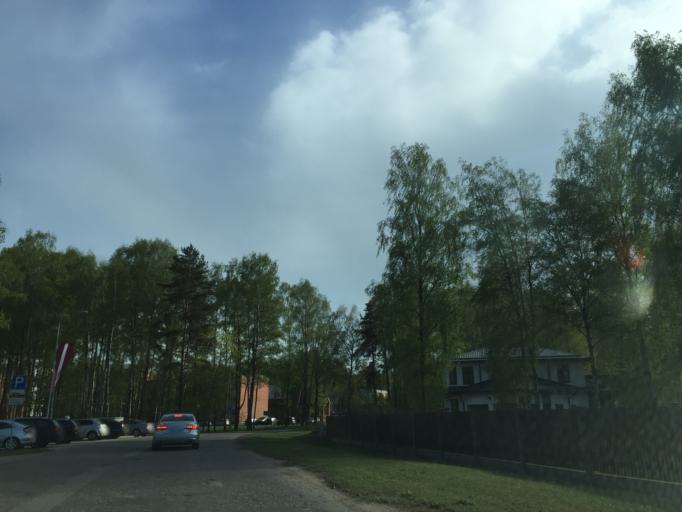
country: LV
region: Kekava
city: Balozi
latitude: 56.8824
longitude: 24.1499
